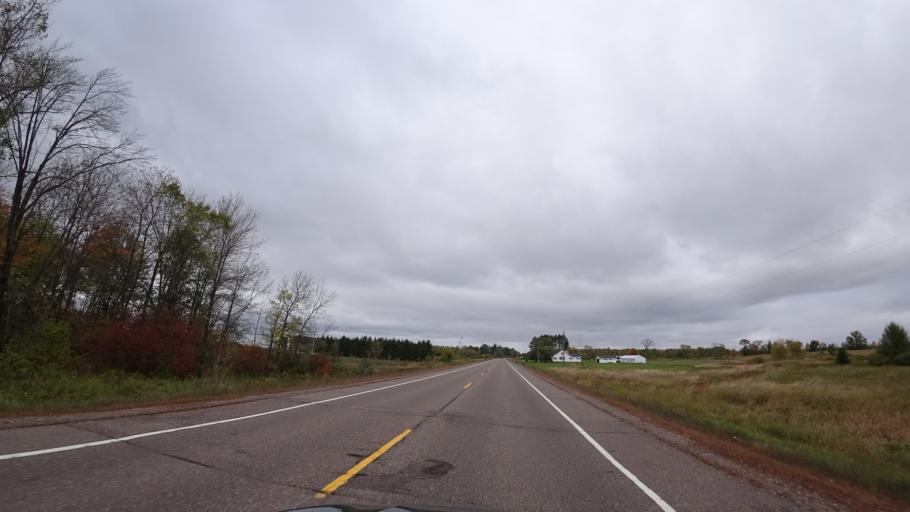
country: US
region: Wisconsin
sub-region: Rusk County
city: Ladysmith
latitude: 45.5479
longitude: -91.1117
